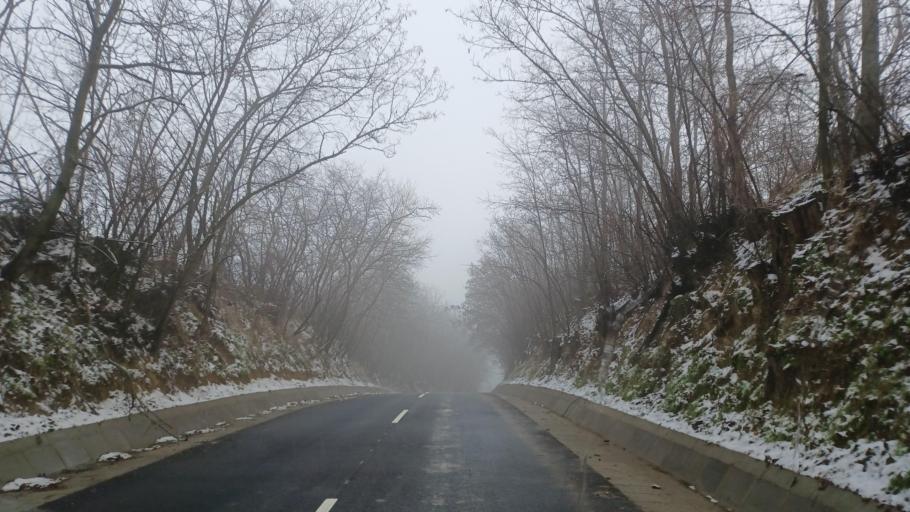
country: HU
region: Tolna
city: Gyonk
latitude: 46.5767
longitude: 18.4743
